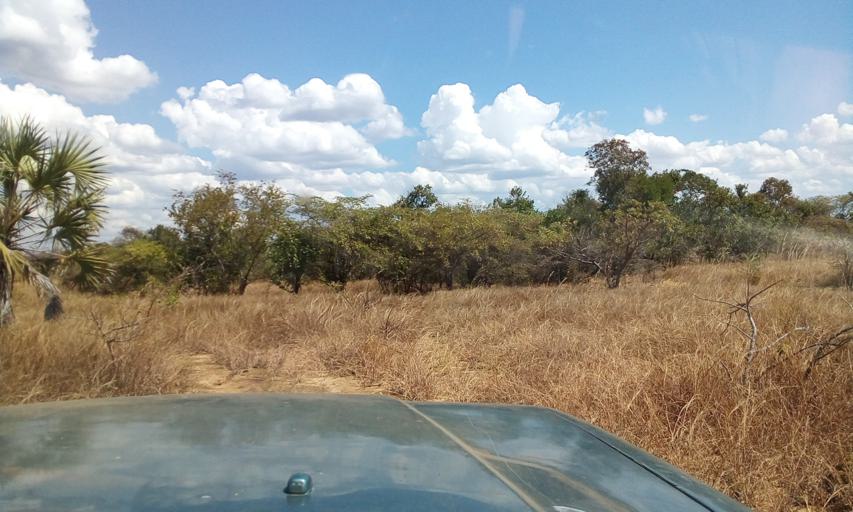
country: MG
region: Melaky
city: Mahabe
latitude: -16.4376
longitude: 45.3793
